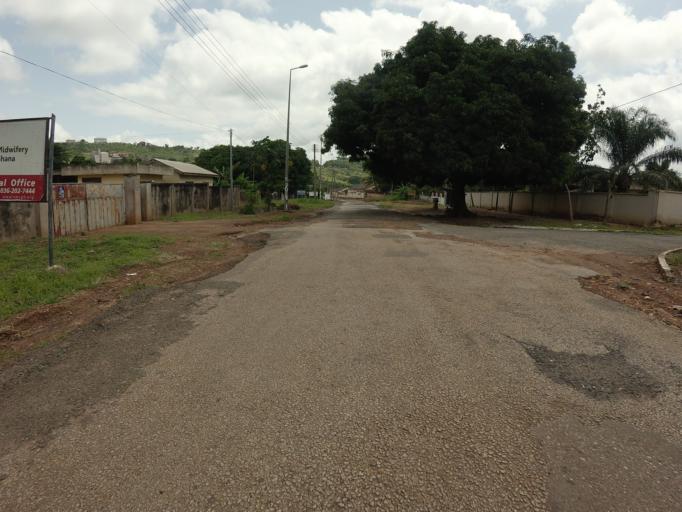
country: GH
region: Volta
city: Ho
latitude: 6.6085
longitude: 0.4609
